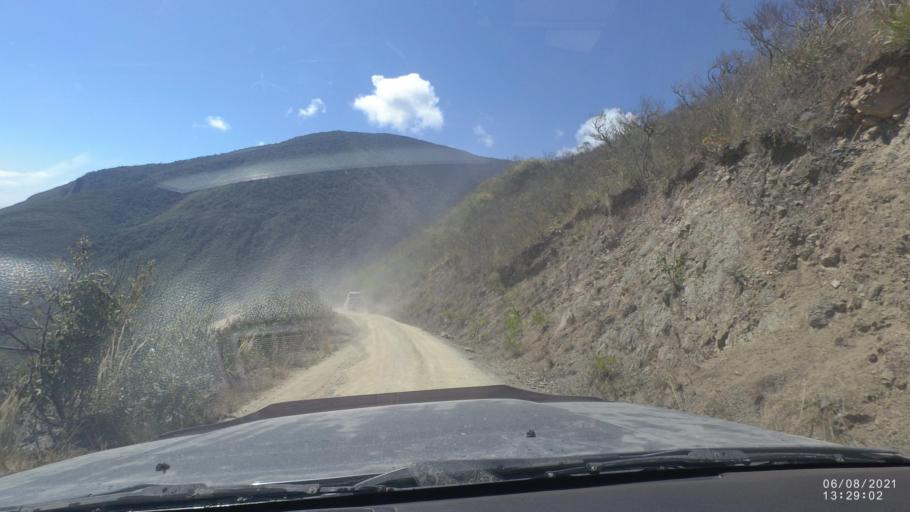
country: BO
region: La Paz
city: Quime
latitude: -16.6985
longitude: -66.7230
